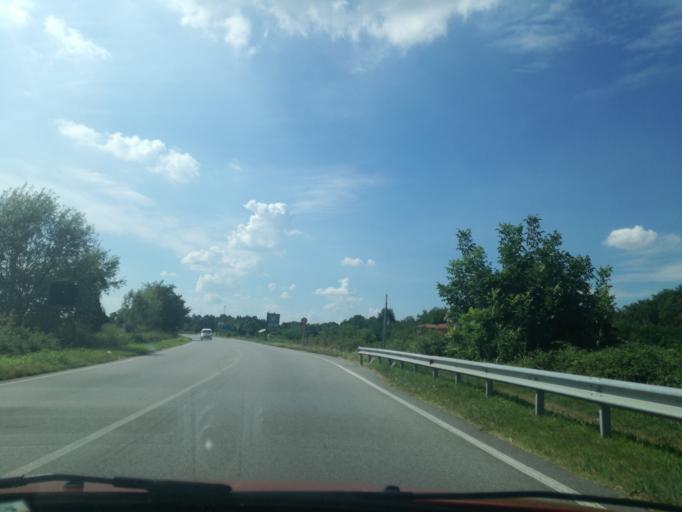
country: IT
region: Lombardy
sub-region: Citta metropolitana di Milano
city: Trezzo sull'Adda
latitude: 45.6084
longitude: 9.5051
